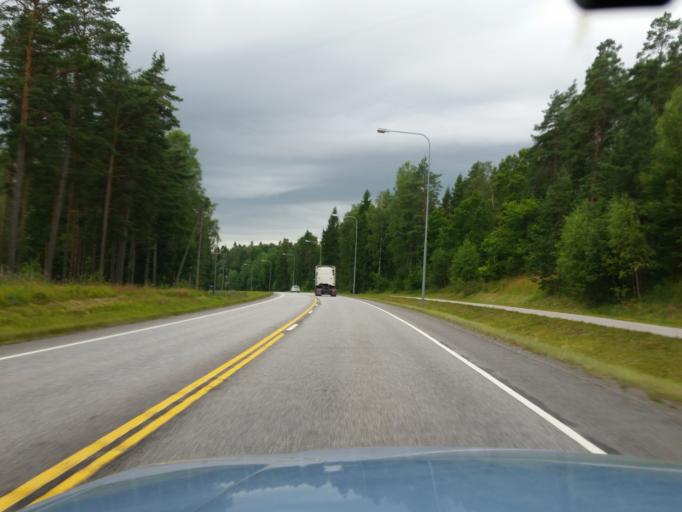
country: FI
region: Uusimaa
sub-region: Raaseporin
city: Ekenaes
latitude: 59.9835
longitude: 23.4066
